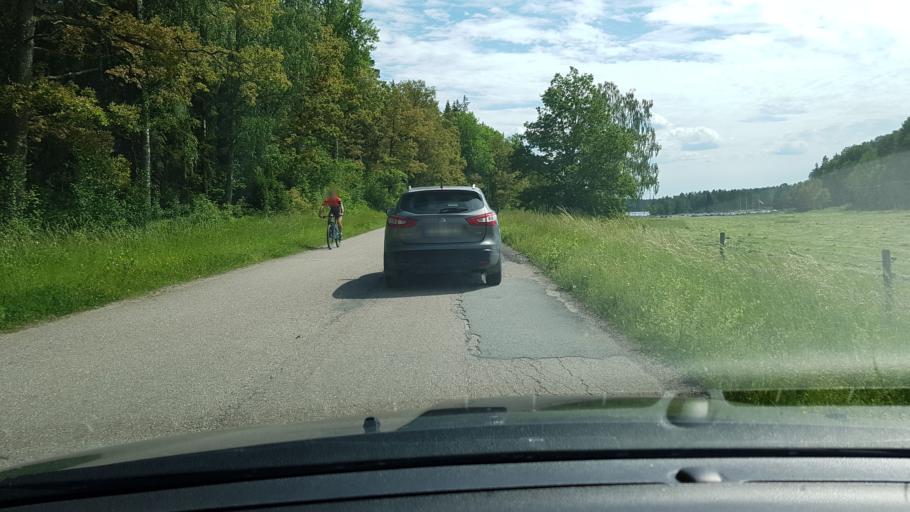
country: SE
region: Uppsala
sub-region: Knivsta Kommun
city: Knivsta
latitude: 59.8418
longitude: 17.9149
